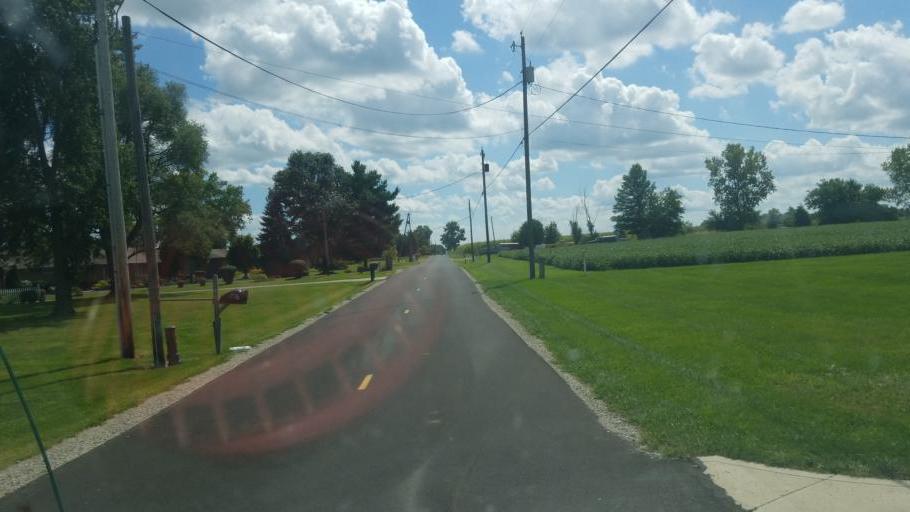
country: US
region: Ohio
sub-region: Marion County
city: Prospect
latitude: 40.5107
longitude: -83.1657
